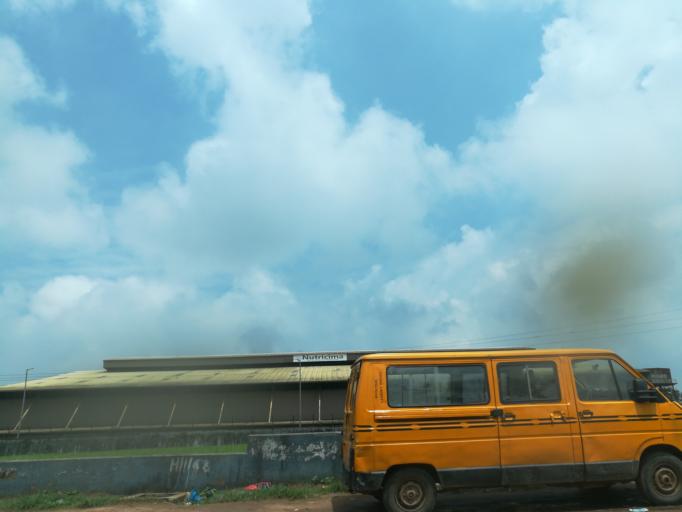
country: NG
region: Lagos
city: Ikorodu
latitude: 6.6722
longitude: 3.5125
